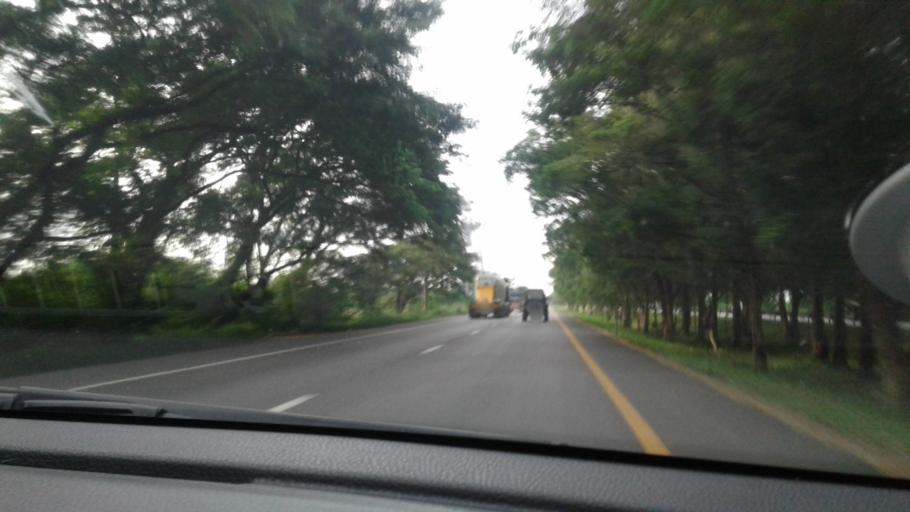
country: TH
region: Prachuap Khiri Khan
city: Pran Buri
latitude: 12.4398
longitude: 99.9101
